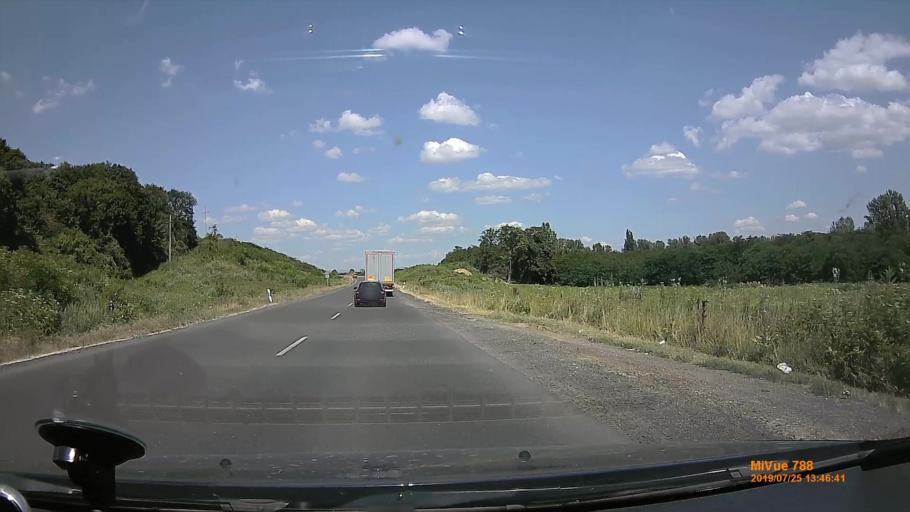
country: HU
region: Borsod-Abauj-Zemplen
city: Gonc
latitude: 48.4896
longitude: 21.2139
